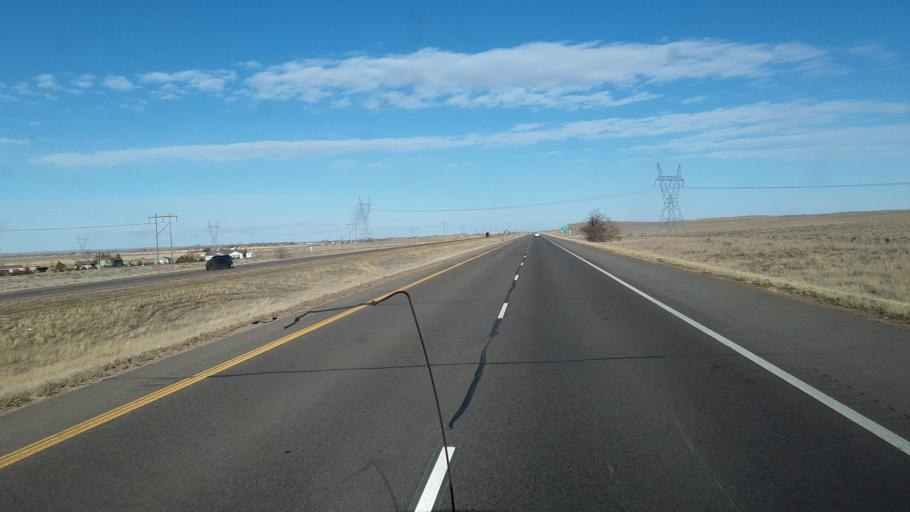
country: US
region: Colorado
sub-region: Morgan County
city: Brush
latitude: 40.2883
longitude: -103.5496
